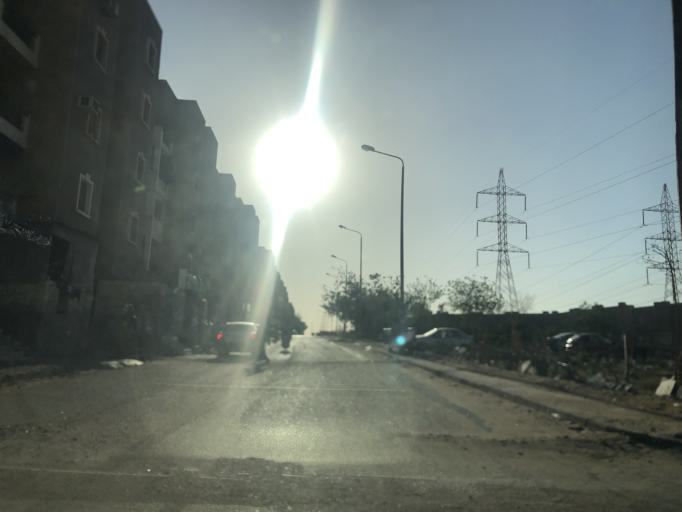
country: EG
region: Al Jizah
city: Al Jizah
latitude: 29.9887
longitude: 31.1058
